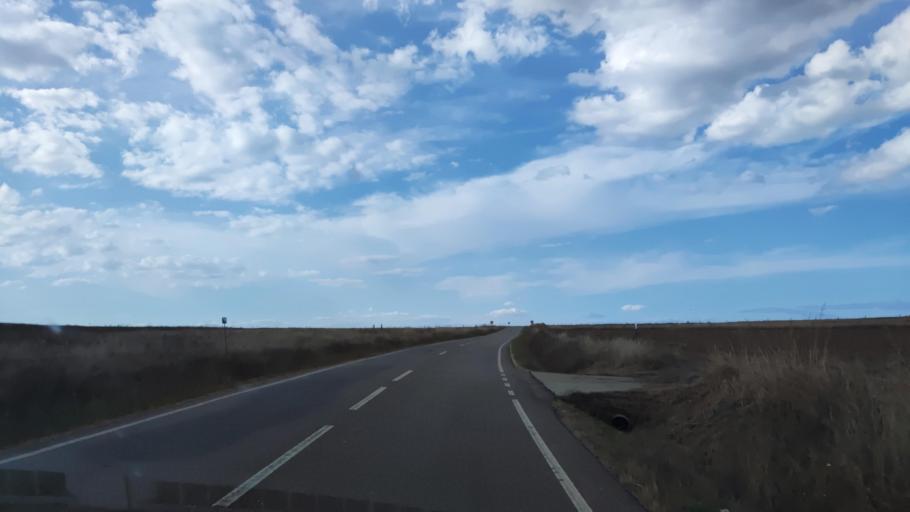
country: ES
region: Castille and Leon
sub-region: Provincia de Salamanca
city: Pastores
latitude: 40.5082
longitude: -6.5046
